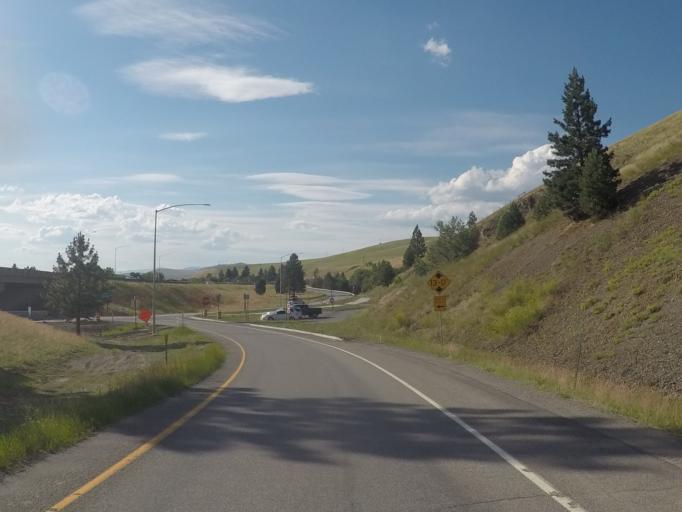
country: US
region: Montana
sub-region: Missoula County
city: Missoula
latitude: 46.8801
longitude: -113.9917
